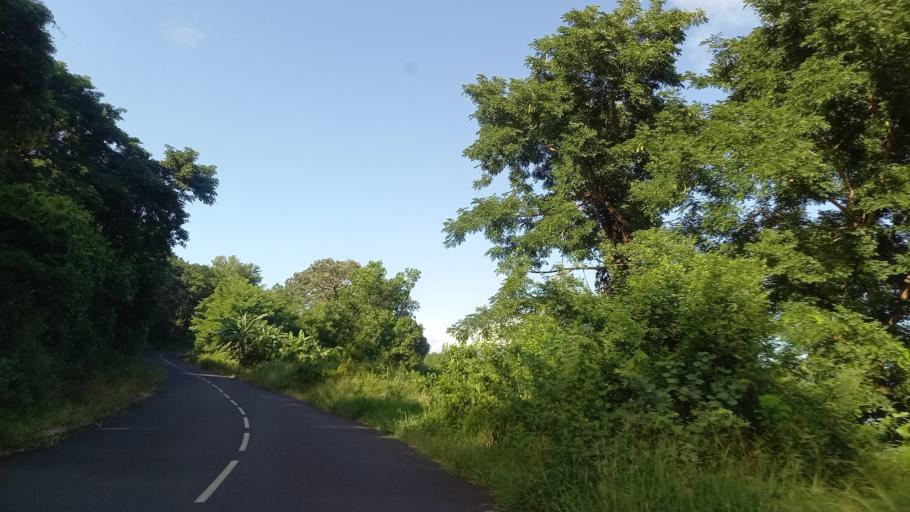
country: YT
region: Kani-Keli
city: Kani Keli
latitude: -12.9772
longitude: 45.1085
